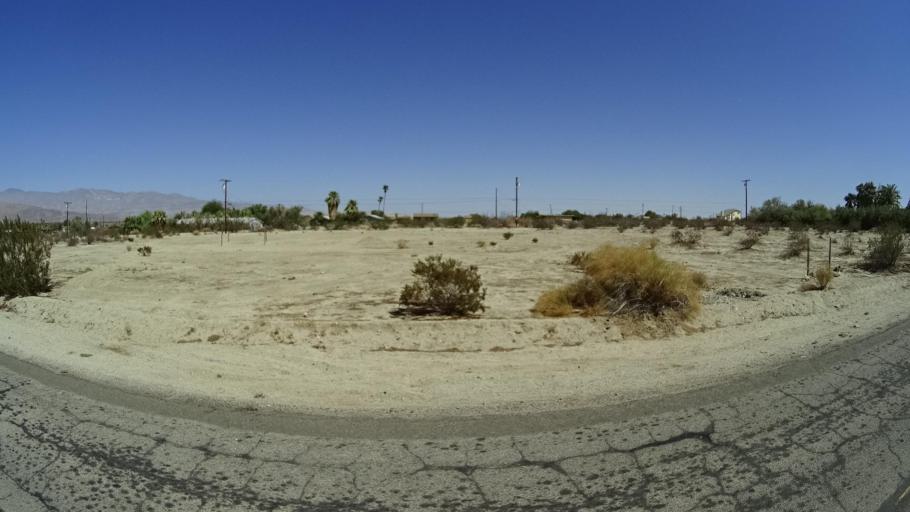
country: US
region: California
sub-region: San Diego County
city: Borrego Springs
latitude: 33.2391
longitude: -116.3762
